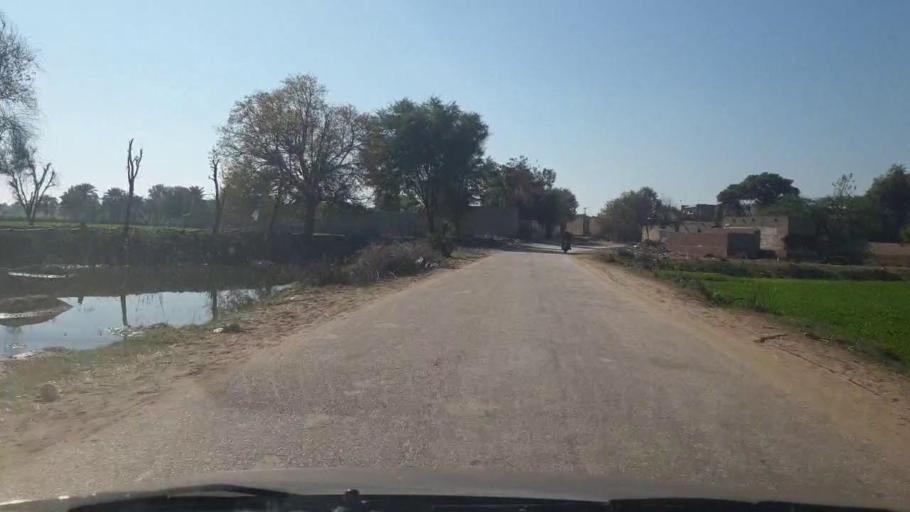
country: PK
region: Sindh
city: Bozdar
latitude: 27.0970
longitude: 68.6281
